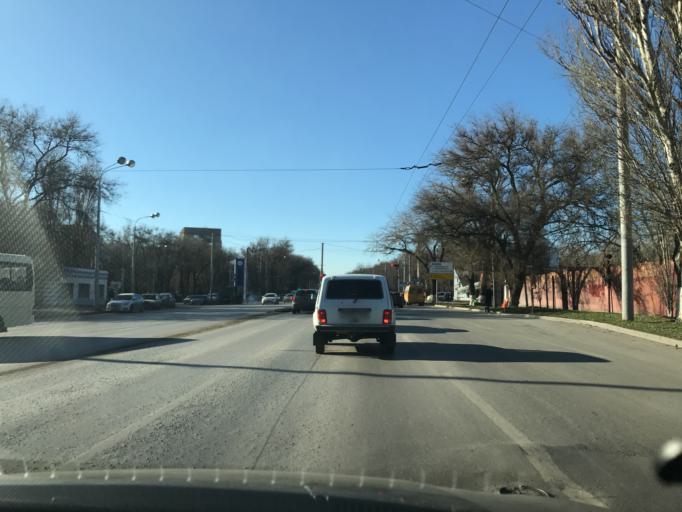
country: RU
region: Rostov
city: Rostov-na-Donu
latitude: 47.2122
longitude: 39.6477
